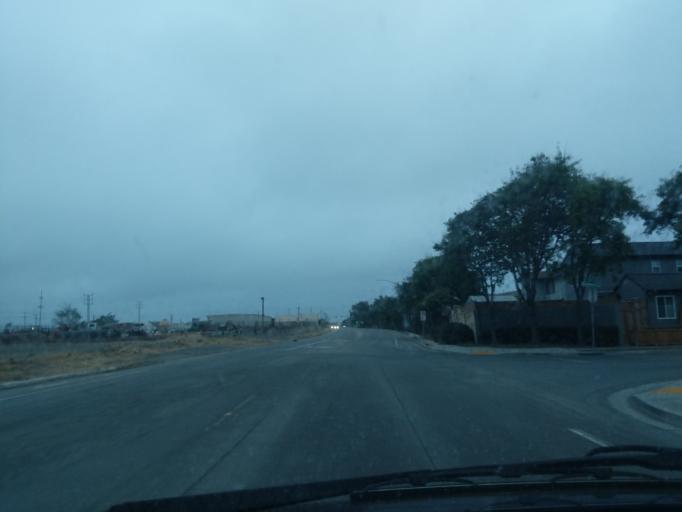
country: US
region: California
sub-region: Monterey County
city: Salinas
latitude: 36.6827
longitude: -121.6582
